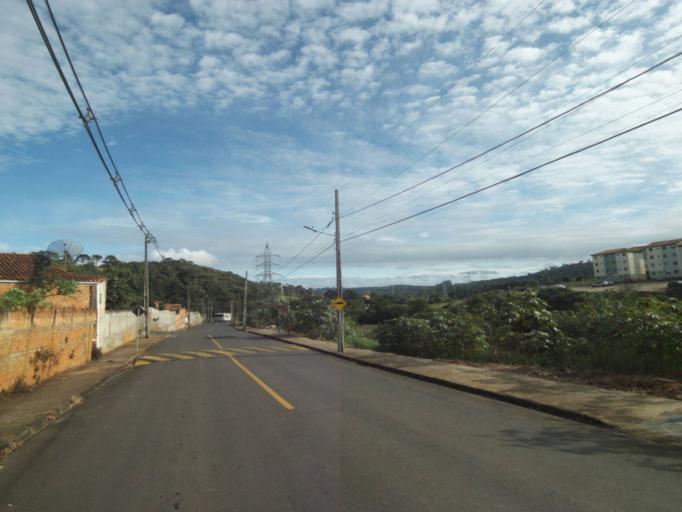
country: BR
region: Parana
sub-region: Telemaco Borba
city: Telemaco Borba
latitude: -24.3442
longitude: -50.6057
